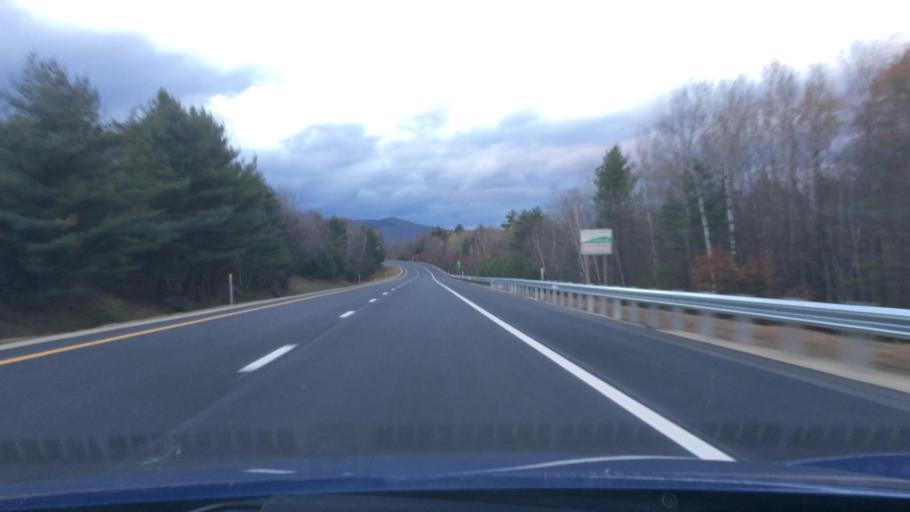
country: US
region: New Hampshire
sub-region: Grafton County
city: Thornton
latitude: 43.8895
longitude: -71.6816
